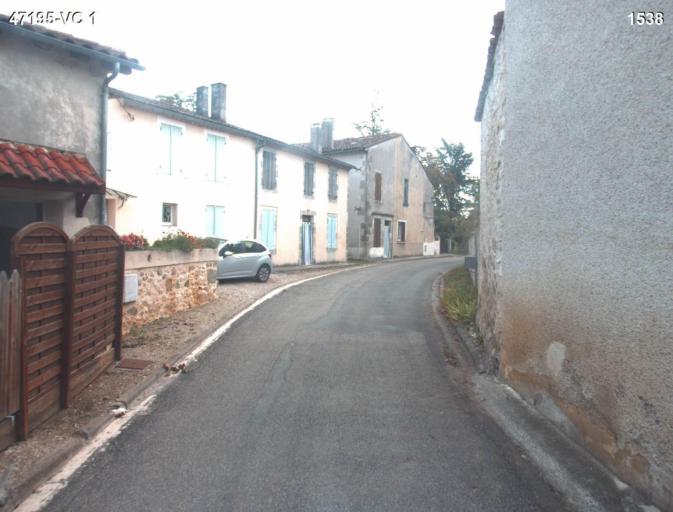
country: FR
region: Aquitaine
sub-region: Departement du Lot-et-Garonne
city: Nerac
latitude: 44.1212
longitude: 0.3498
